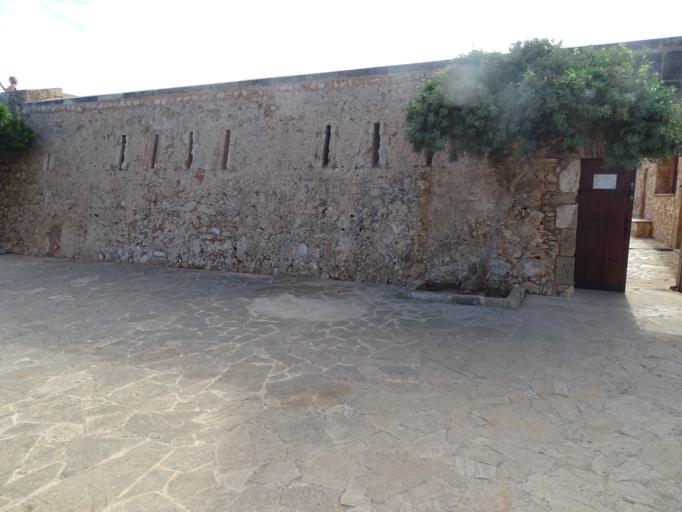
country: ES
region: Balearic Islands
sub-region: Illes Balears
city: Santanyi
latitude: 39.3669
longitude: 3.2336
